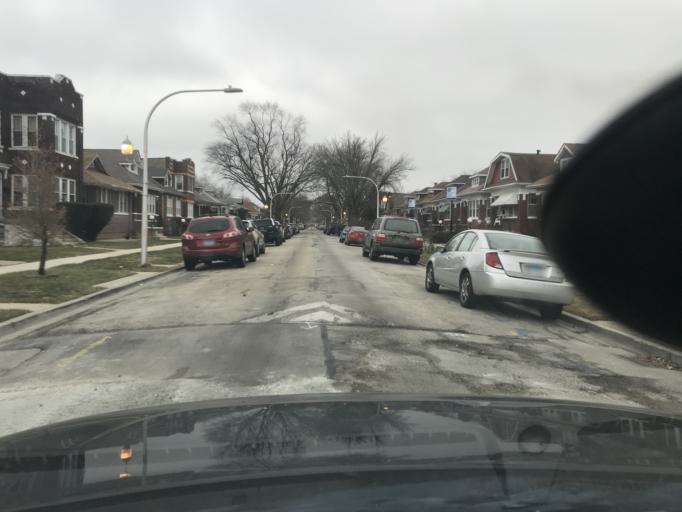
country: US
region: Indiana
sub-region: Lake County
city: Whiting
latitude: 41.7439
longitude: -87.5685
